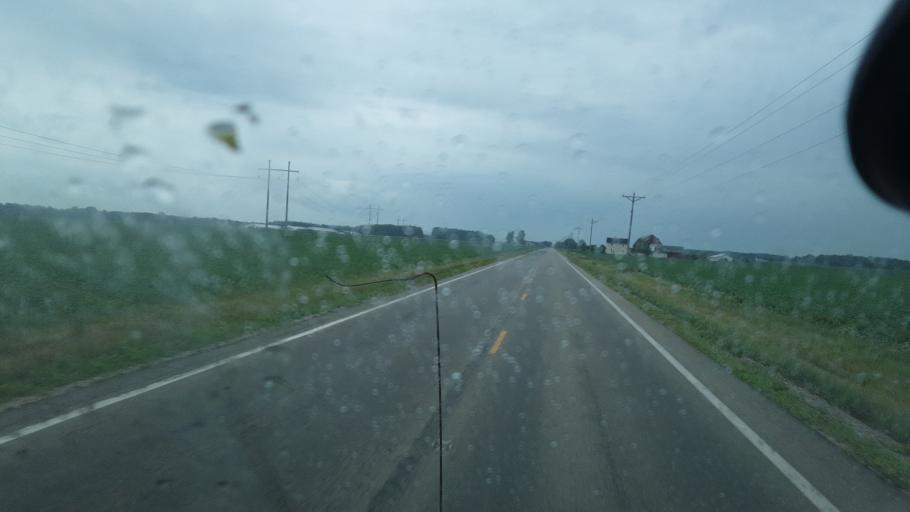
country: US
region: Ohio
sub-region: Defiance County
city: Hicksville
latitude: 41.2961
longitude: -84.6830
